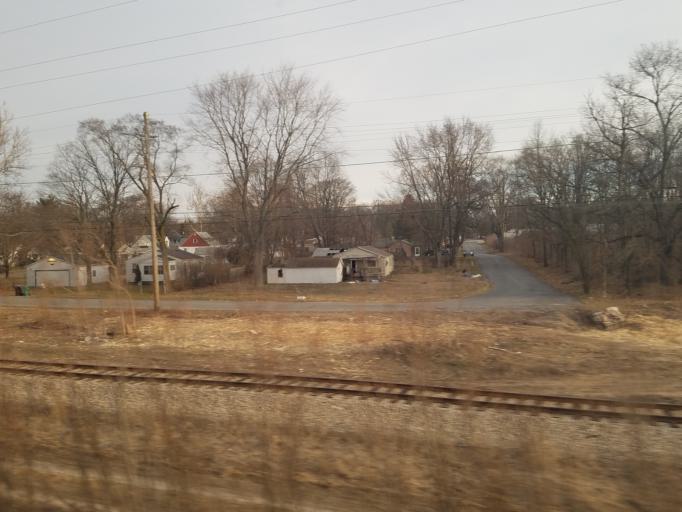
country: US
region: Indiana
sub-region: Saint Joseph County
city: South Bend
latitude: 41.6836
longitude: -86.3124
